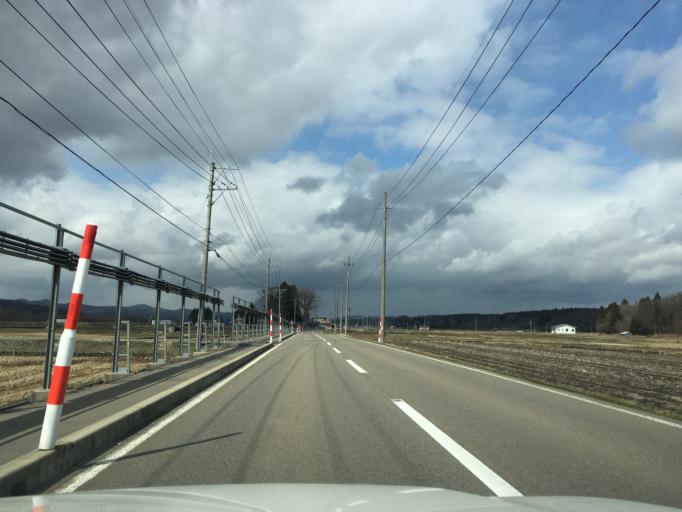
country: JP
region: Akita
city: Takanosu
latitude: 40.1322
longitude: 140.3582
